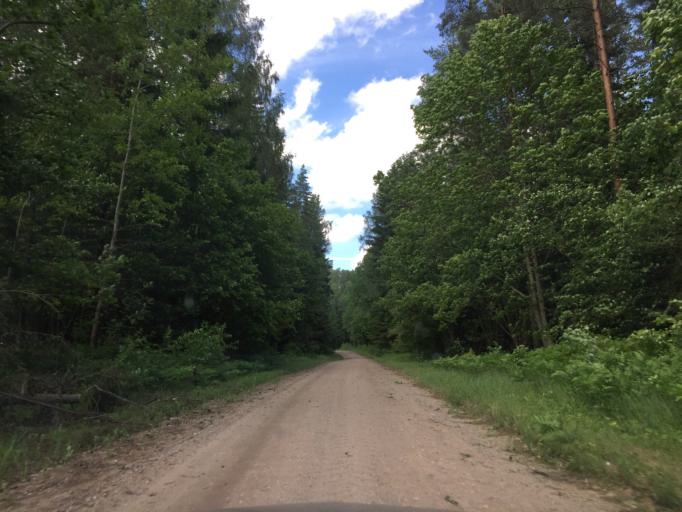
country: LV
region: Engure
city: Smarde
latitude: 56.9888
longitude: 23.2843
